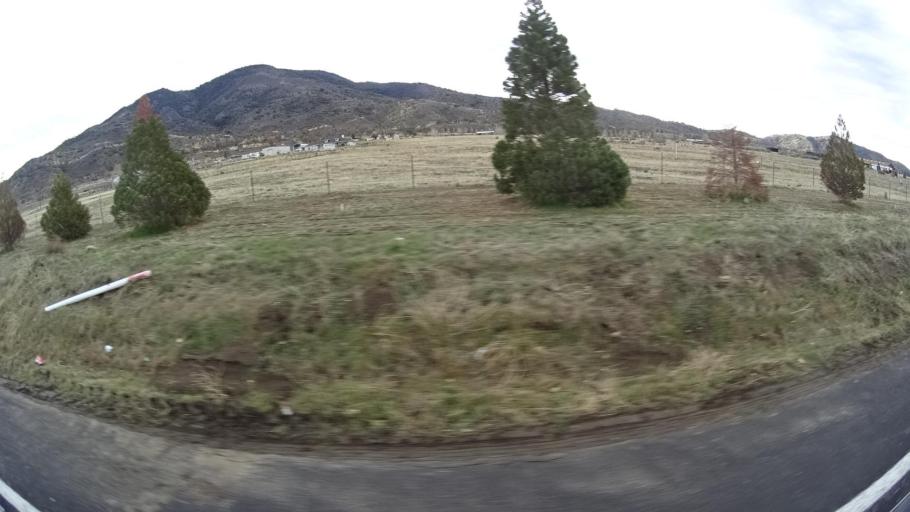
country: US
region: California
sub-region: Kern County
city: Stallion Springs
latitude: 35.0956
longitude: -118.6060
